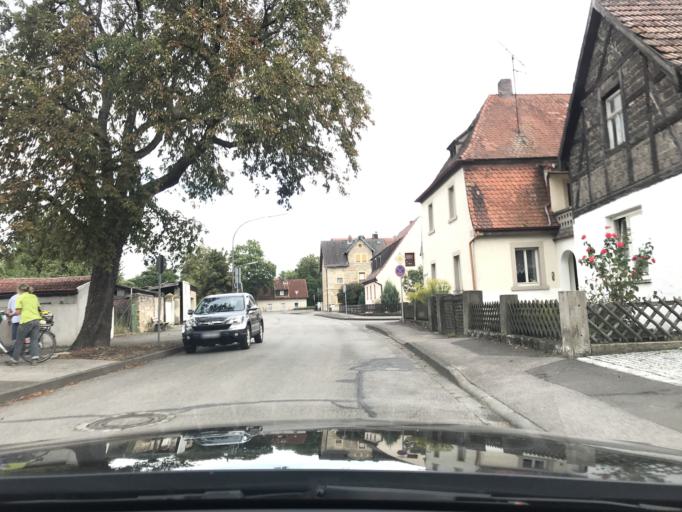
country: DE
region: Bavaria
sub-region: Regierungsbezirk Unterfranken
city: Zeil
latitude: 50.0083
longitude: 10.5935
